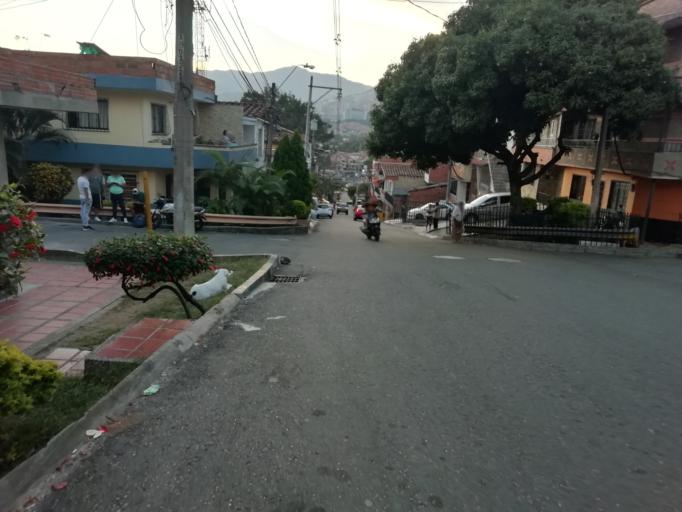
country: CO
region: Antioquia
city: Medellin
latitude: 6.2749
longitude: -75.5615
